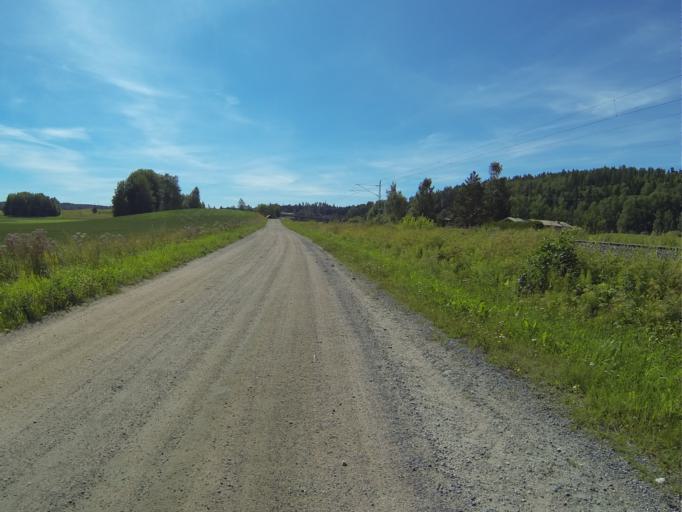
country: FI
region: Varsinais-Suomi
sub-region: Salo
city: Salo
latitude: 60.3091
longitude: 23.1074
